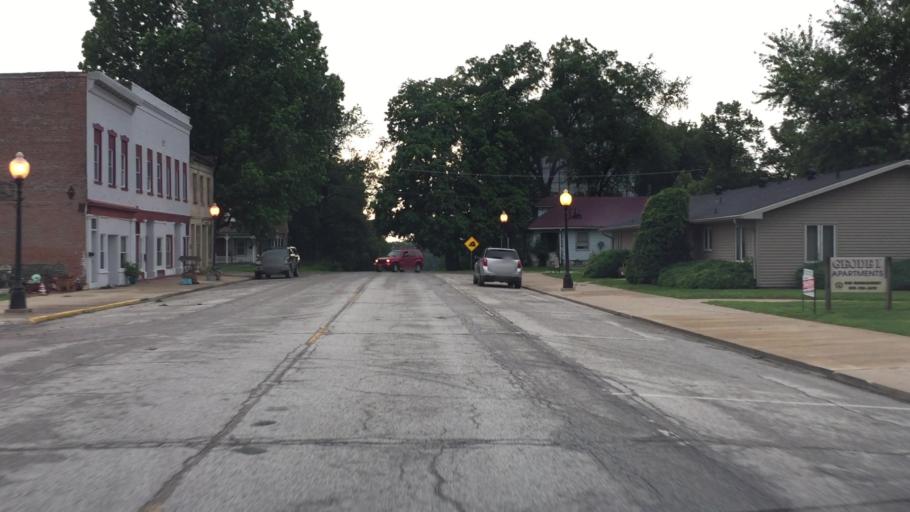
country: US
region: Illinois
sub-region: Hancock County
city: Warsaw
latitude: 40.3606
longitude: -91.4387
